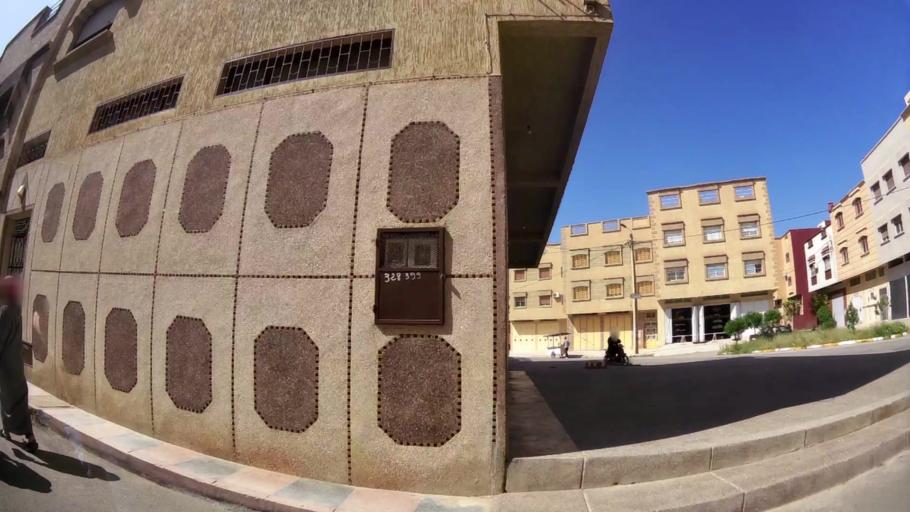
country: MA
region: Oriental
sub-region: Oujda-Angad
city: Oujda
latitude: 34.6772
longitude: -1.9343
